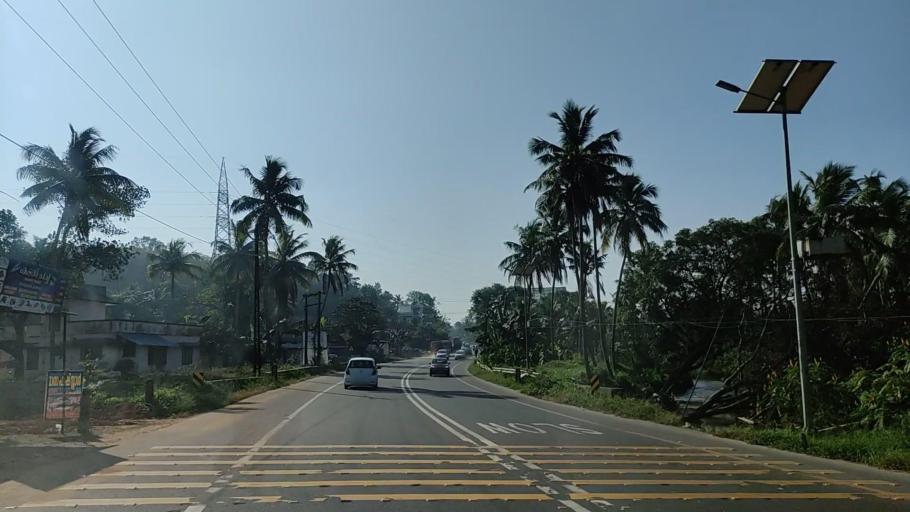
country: IN
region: Kerala
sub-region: Kollam
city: Punalur
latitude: 8.9050
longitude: 76.8555
